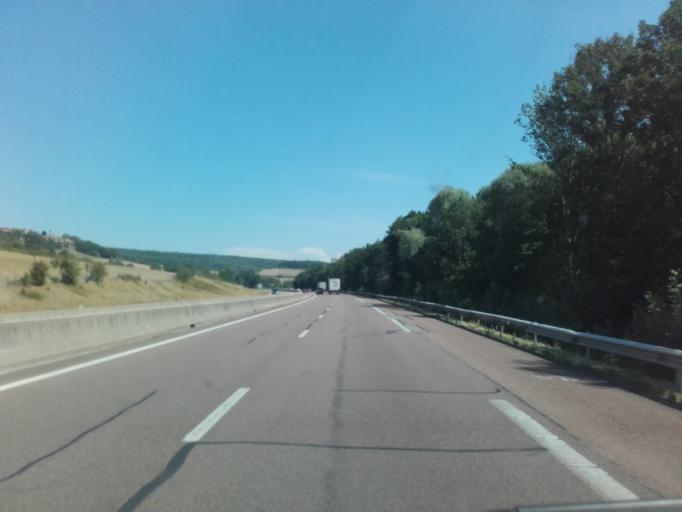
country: FR
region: Bourgogne
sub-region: Departement de la Cote-d'Or
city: Pouilly-en-Auxois
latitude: 47.2007
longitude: 4.6510
